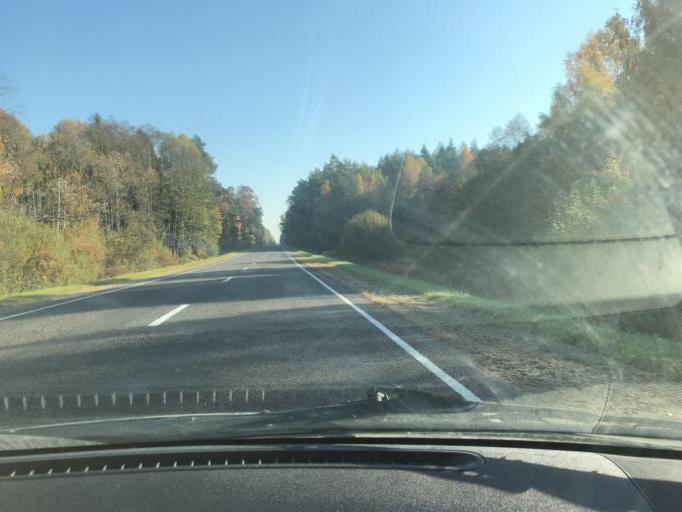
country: BY
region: Brest
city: Lyakhavichy
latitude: 52.9523
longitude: 26.2092
